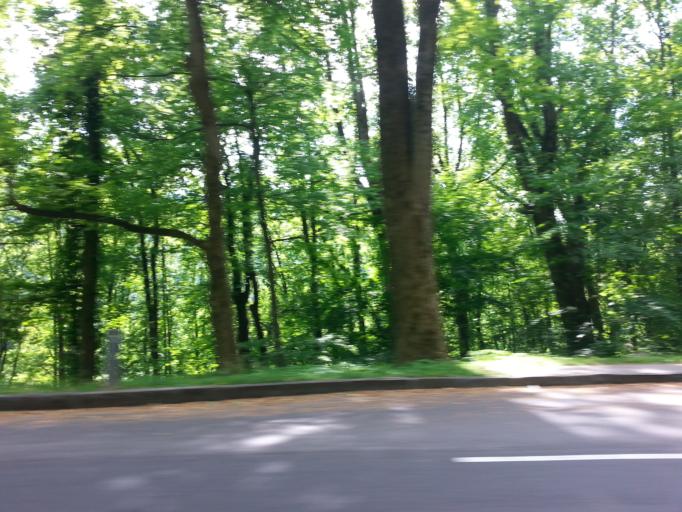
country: US
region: Tennessee
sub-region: Sevier County
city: Gatlinburg
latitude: 35.6397
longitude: -83.4949
